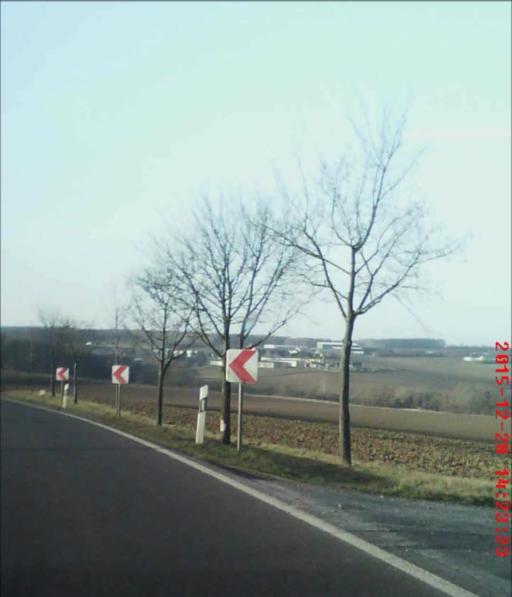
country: DE
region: Thuringia
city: Goldbach
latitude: 51.0542
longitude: 11.4611
